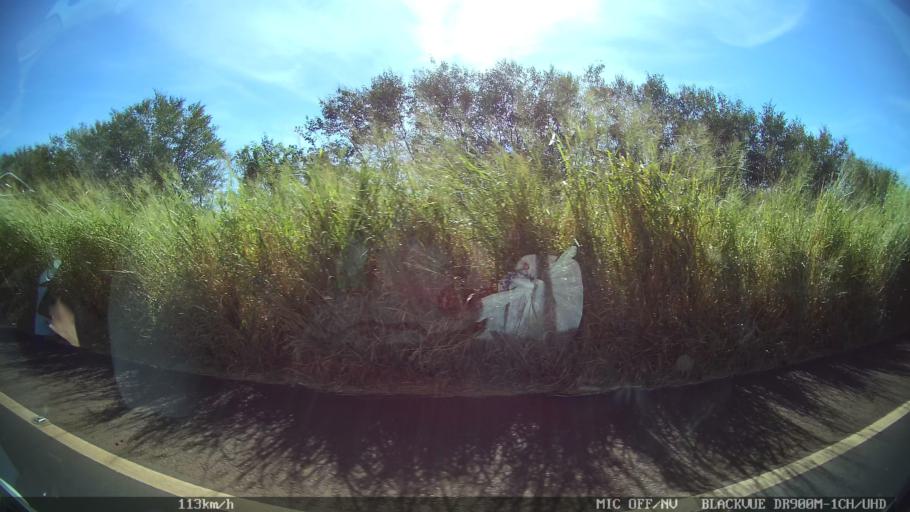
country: BR
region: Sao Paulo
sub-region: Franca
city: Franca
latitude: -20.5582
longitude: -47.5985
